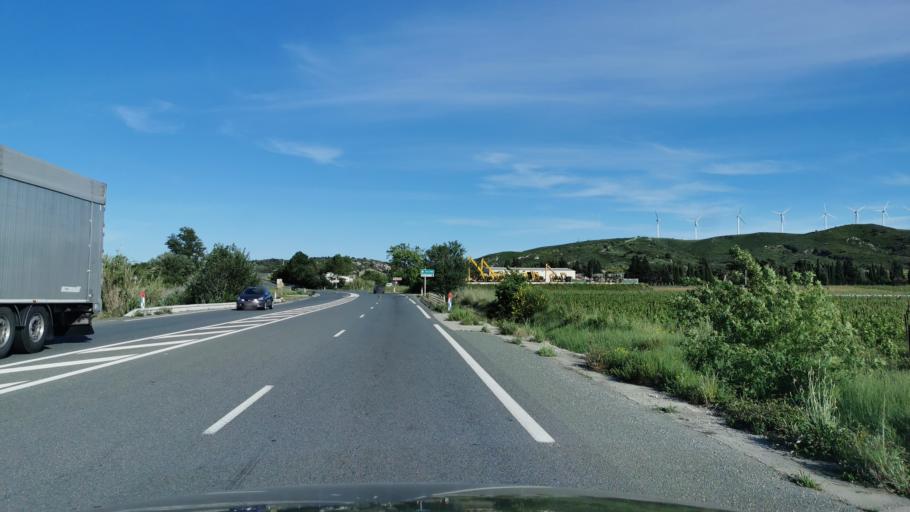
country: FR
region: Languedoc-Roussillon
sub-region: Departement de l'Aude
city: Canet
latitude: 43.2129
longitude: 2.8675
